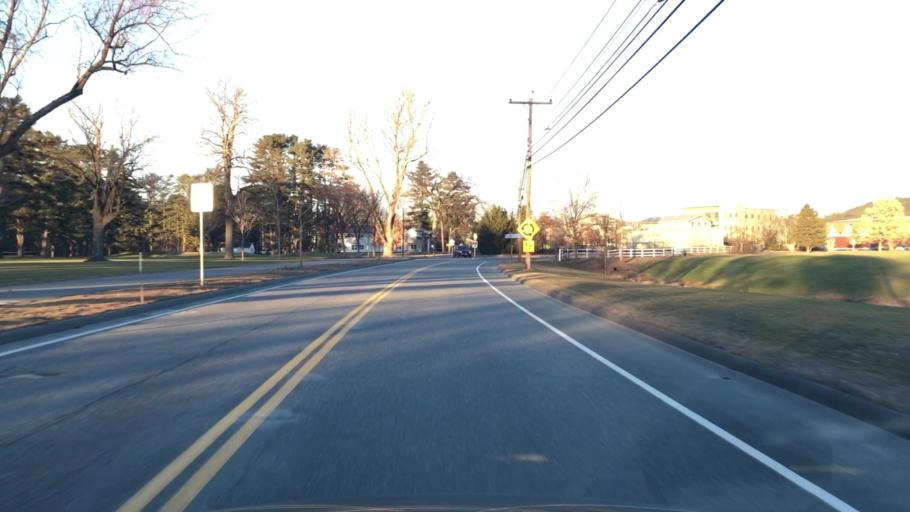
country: US
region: New Hampshire
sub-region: Grafton County
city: Hanover
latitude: 43.7171
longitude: -72.2751
